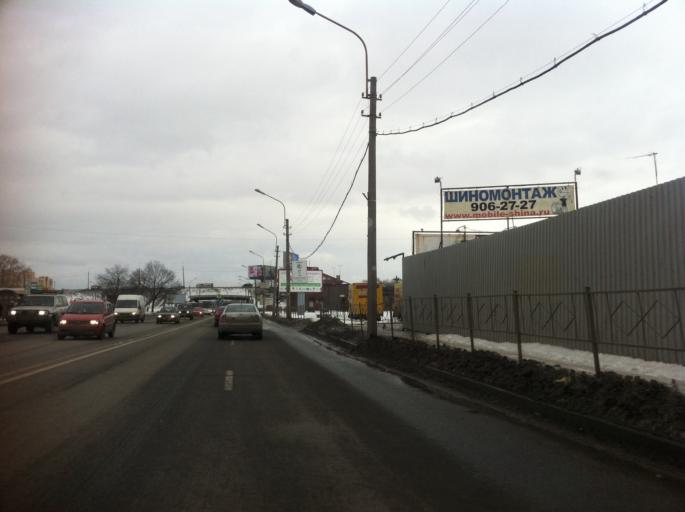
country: RU
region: St.-Petersburg
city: Uritsk
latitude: 59.8240
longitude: 30.1797
